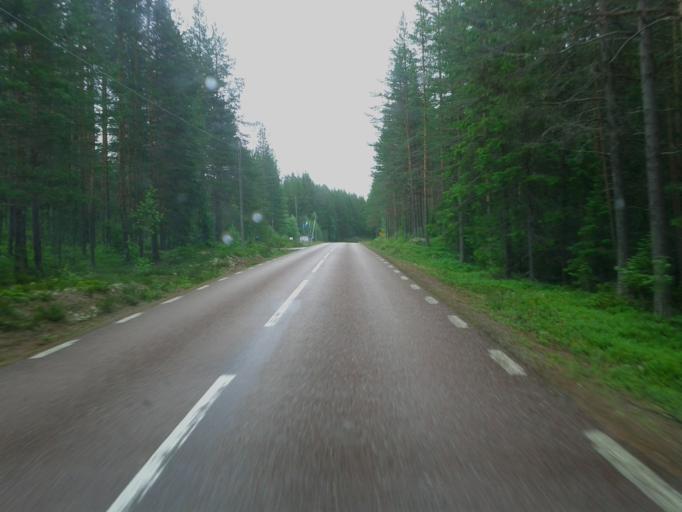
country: NO
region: Hedmark
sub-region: Trysil
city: Innbygda
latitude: 61.8272
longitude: 12.8715
